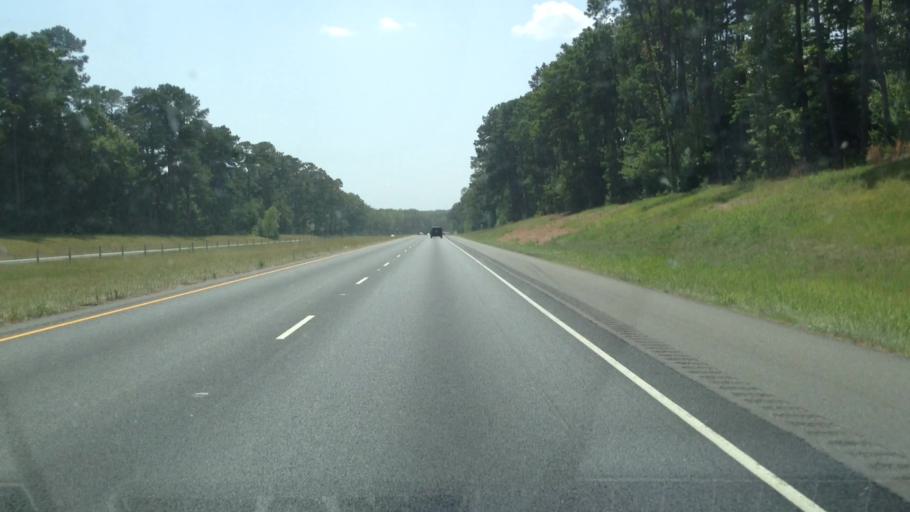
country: US
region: Louisiana
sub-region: Webster Parish
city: Minden
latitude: 32.5621
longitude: -93.1387
